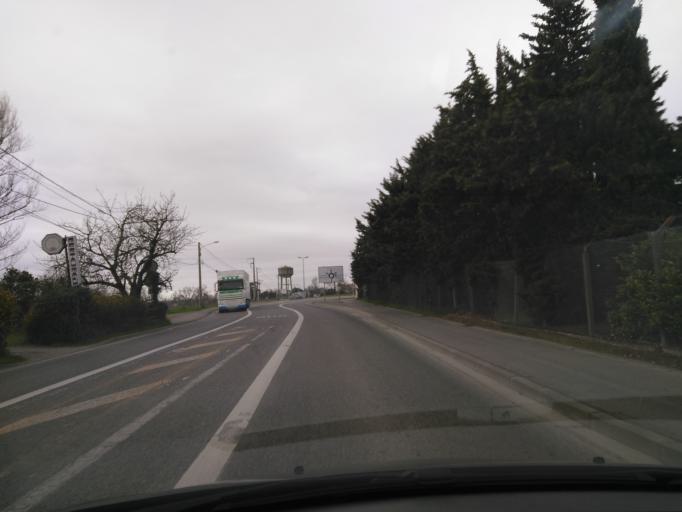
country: FR
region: Midi-Pyrenees
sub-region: Departement de la Haute-Garonne
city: Cugnaux
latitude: 43.5369
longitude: 1.3673
